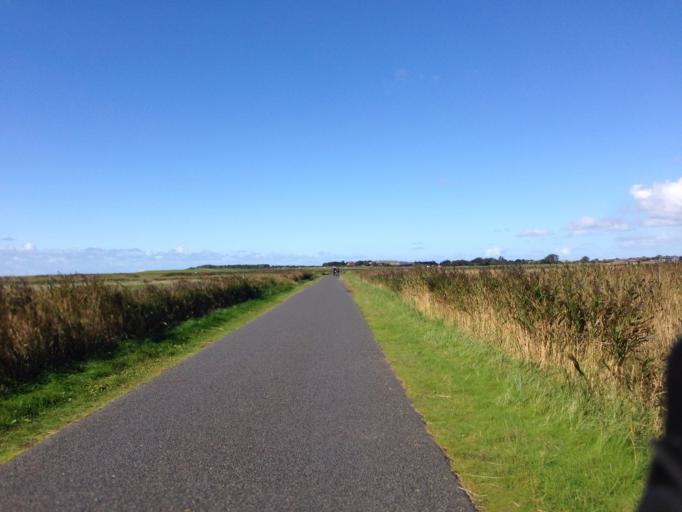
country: DE
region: Schleswig-Holstein
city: Witsum
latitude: 54.6966
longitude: 8.4287
